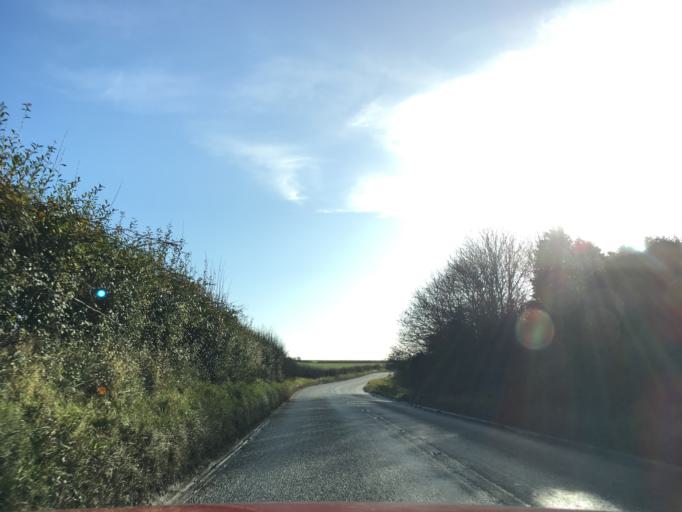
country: GB
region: England
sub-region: Wiltshire
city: Collingbourne Kingston
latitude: 51.2737
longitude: -1.6493
